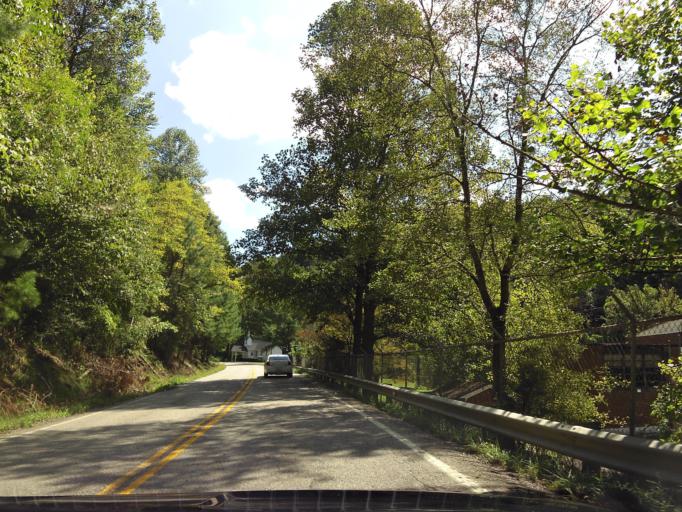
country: US
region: Kentucky
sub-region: Harlan County
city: Loyall
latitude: 36.9565
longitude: -83.3958
